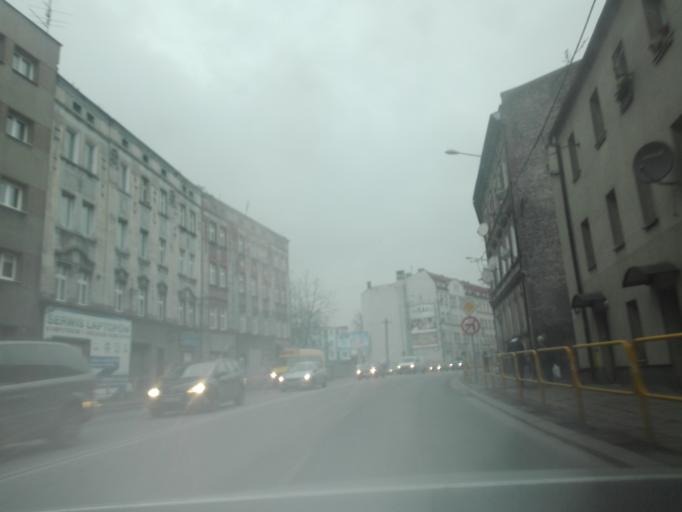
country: PL
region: Silesian Voivodeship
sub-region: Chorzow
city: Chorzow
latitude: 50.2925
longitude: 18.9582
